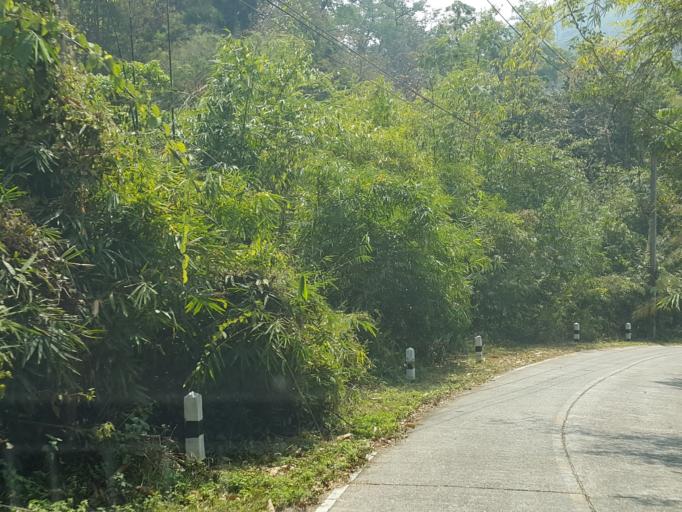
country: TH
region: Lampang
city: Mueang Pan
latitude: 18.8273
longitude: 99.4259
